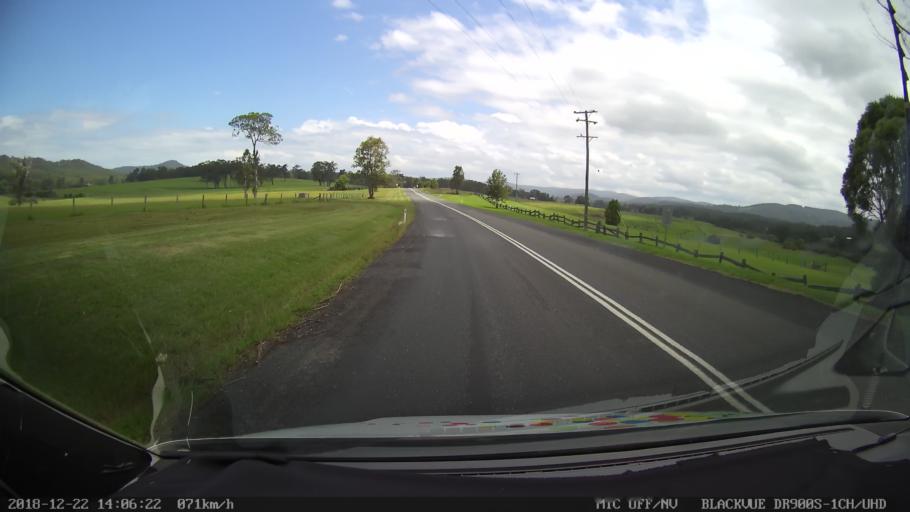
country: AU
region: New South Wales
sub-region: Clarence Valley
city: Coutts Crossing
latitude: -29.9546
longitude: 152.7274
